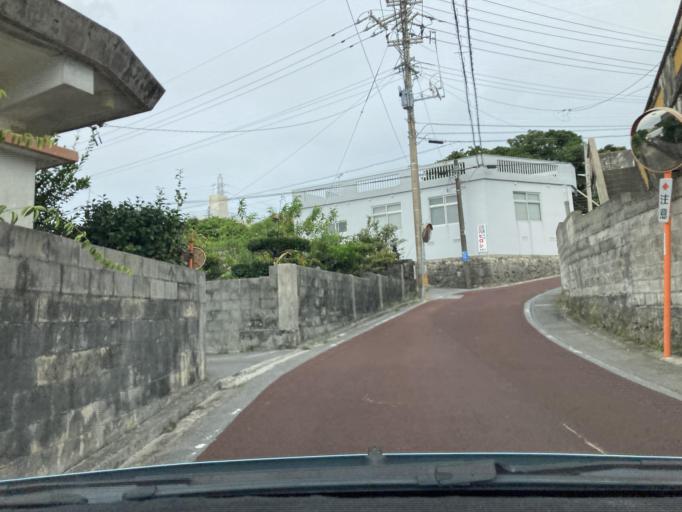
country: JP
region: Okinawa
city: Itoman
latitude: 26.1439
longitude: 127.6781
